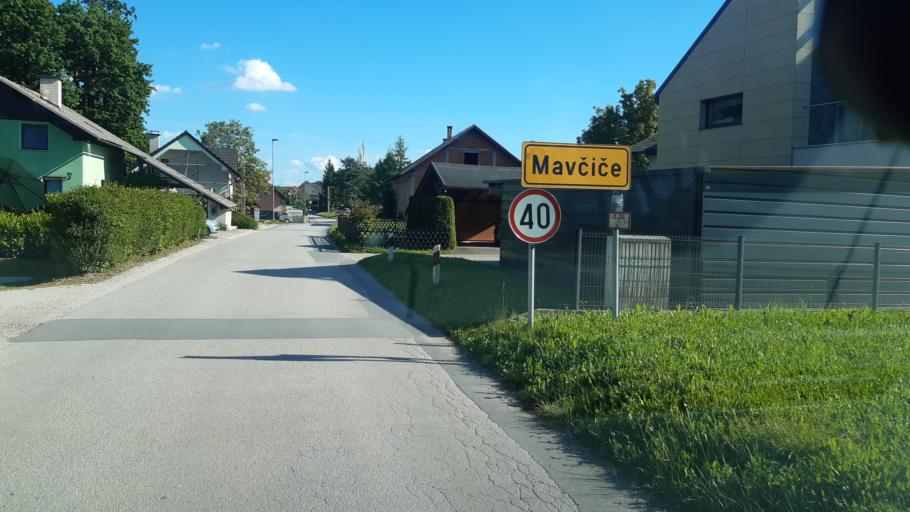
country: SI
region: Sencur
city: Hrastje
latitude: 46.1905
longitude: 14.4032
